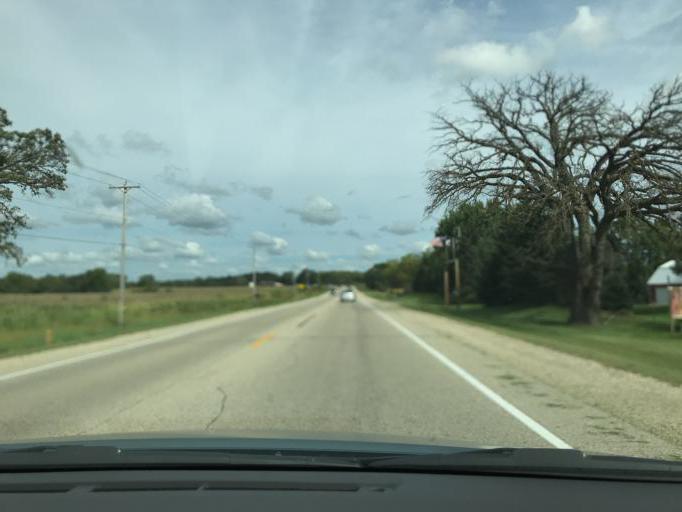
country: US
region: Wisconsin
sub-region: Racine County
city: Bohners Lake
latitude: 42.6365
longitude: -88.2490
